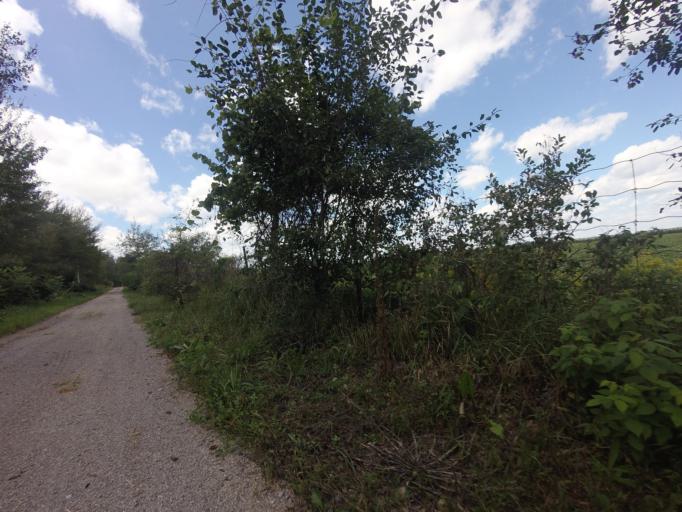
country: CA
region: Ontario
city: Huron East
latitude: 43.6374
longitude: -81.1955
